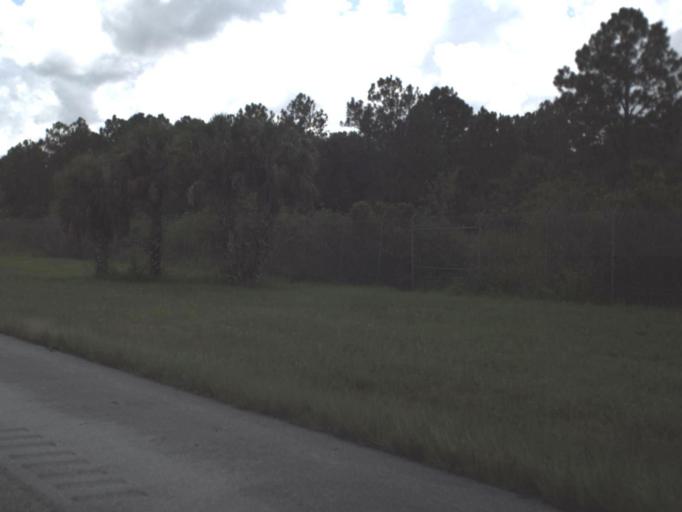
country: US
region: Florida
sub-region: Collier County
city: Orangetree
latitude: 26.1530
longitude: -81.4875
